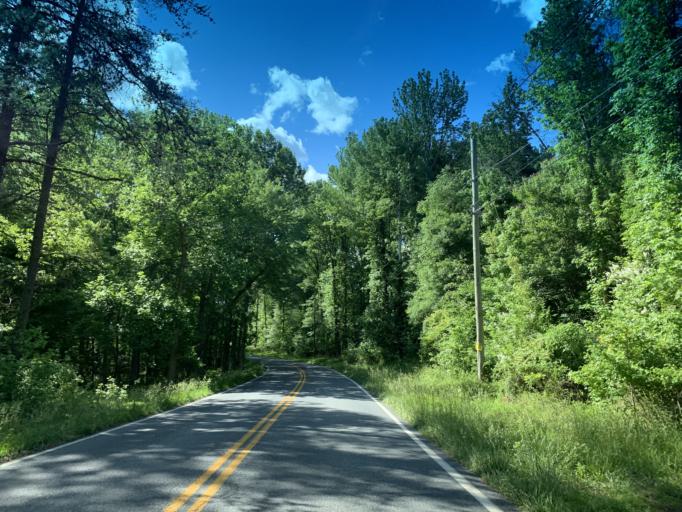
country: US
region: Maryland
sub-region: Cecil County
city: North East
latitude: 39.5639
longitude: -75.9361
